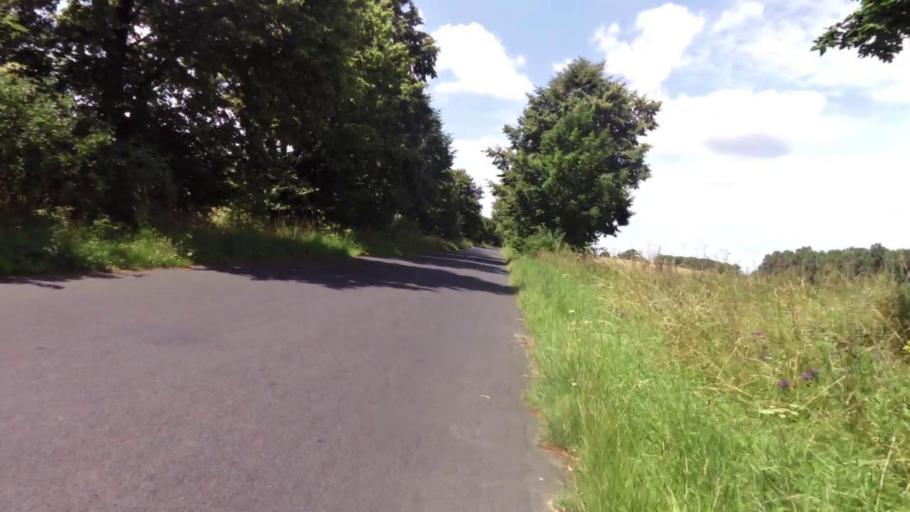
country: PL
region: West Pomeranian Voivodeship
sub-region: Powiat stargardzki
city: Dobrzany
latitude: 53.4286
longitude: 15.4443
